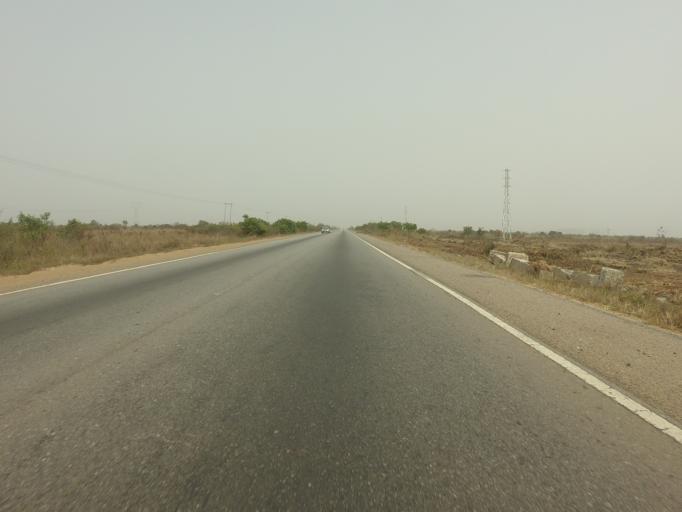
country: GH
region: Greater Accra
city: Tema
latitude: 5.7986
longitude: 0.1341
